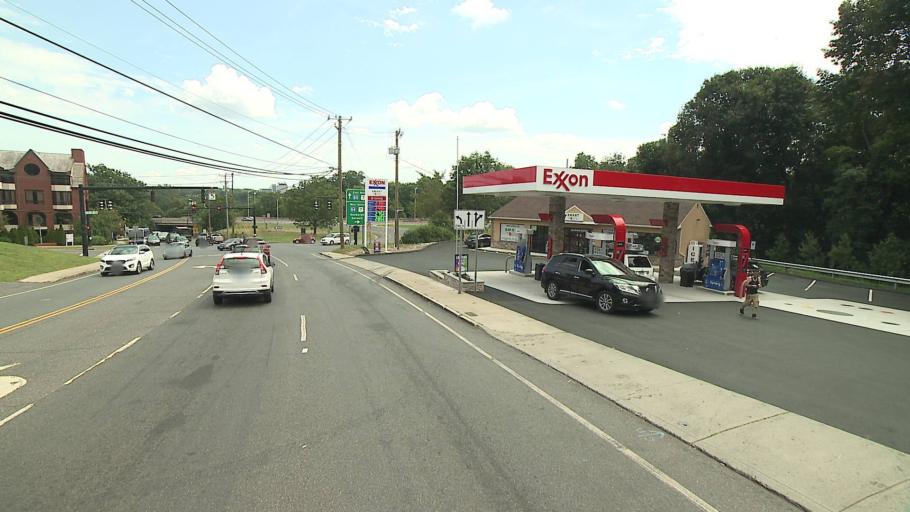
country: US
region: Connecticut
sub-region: Fairfield County
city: Danbury
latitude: 41.4049
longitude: -73.4636
